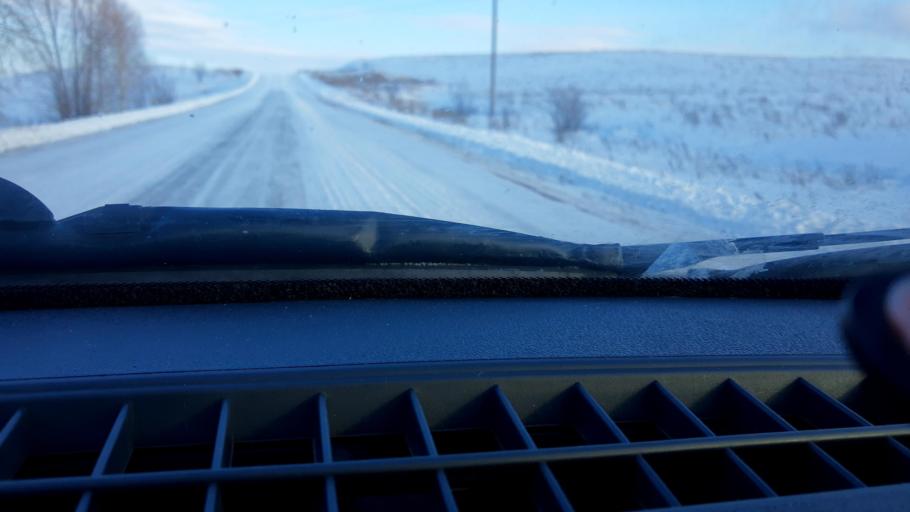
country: RU
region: Bashkortostan
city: Birsk
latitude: 55.1535
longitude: 55.6541
